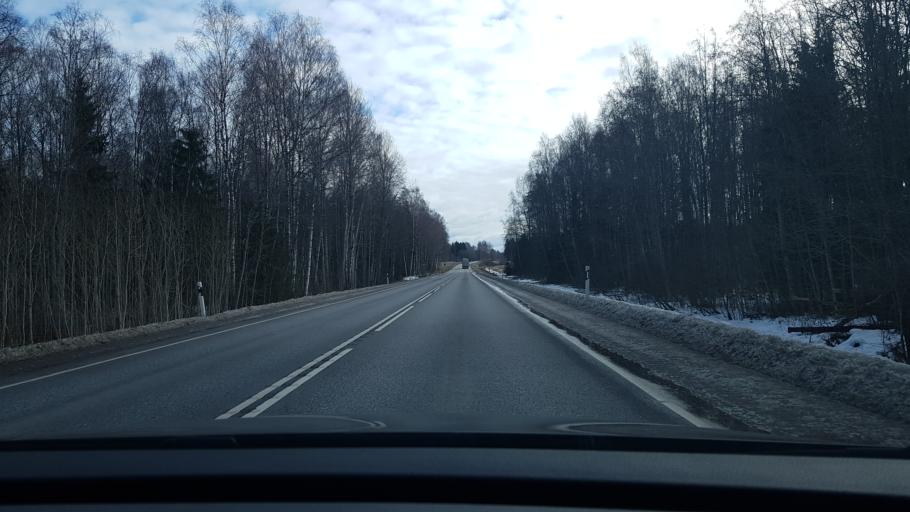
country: EE
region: Viljandimaa
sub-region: Moisakuela linn
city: Moisakula
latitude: 58.1405
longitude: 25.0973
